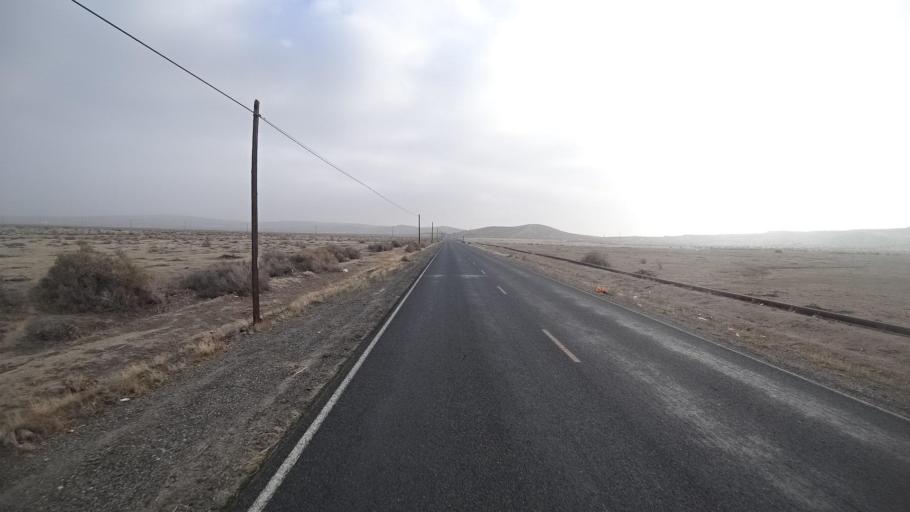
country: US
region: California
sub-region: Kern County
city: Ford City
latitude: 35.1991
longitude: -119.4458
